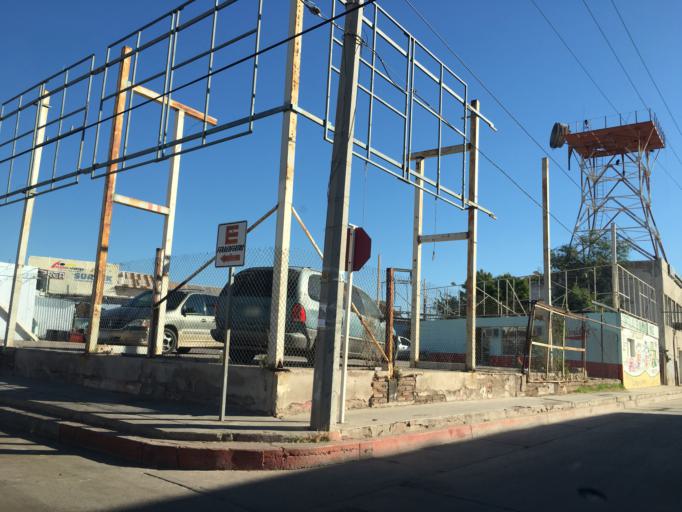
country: MX
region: Sonora
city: Heroica Guaymas
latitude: 27.9211
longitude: -110.8928
